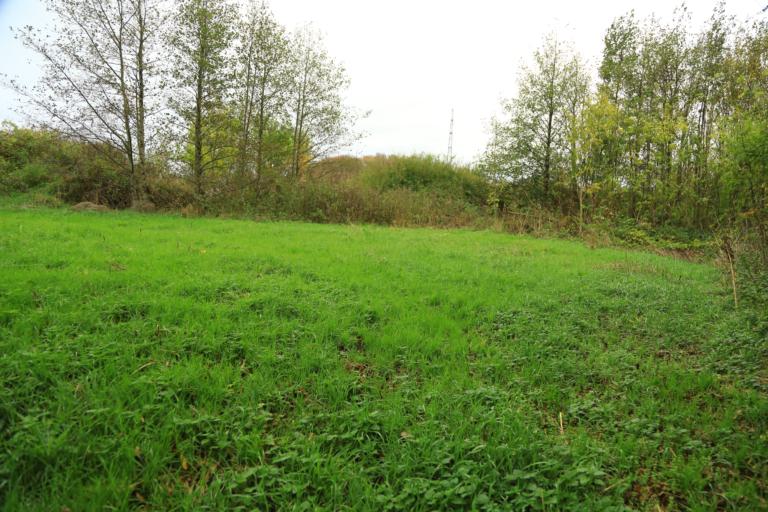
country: SE
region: Halland
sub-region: Varbergs Kommun
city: Varberg
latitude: 57.1274
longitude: 12.3001
